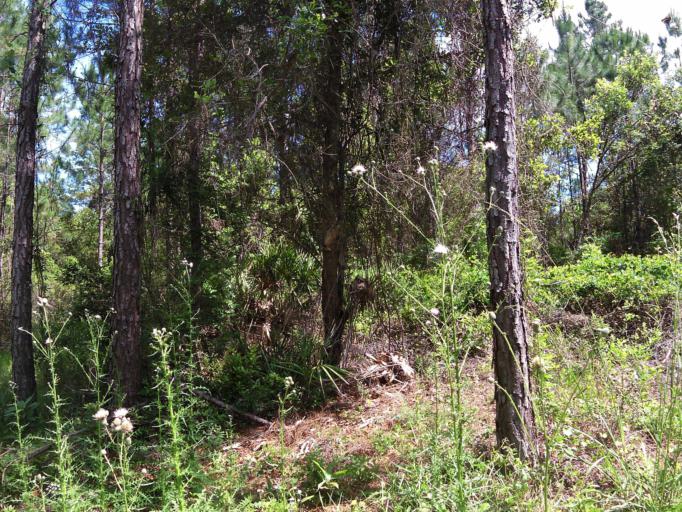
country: US
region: Florida
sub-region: Duval County
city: Atlantic Beach
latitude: 30.4454
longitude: -81.4722
